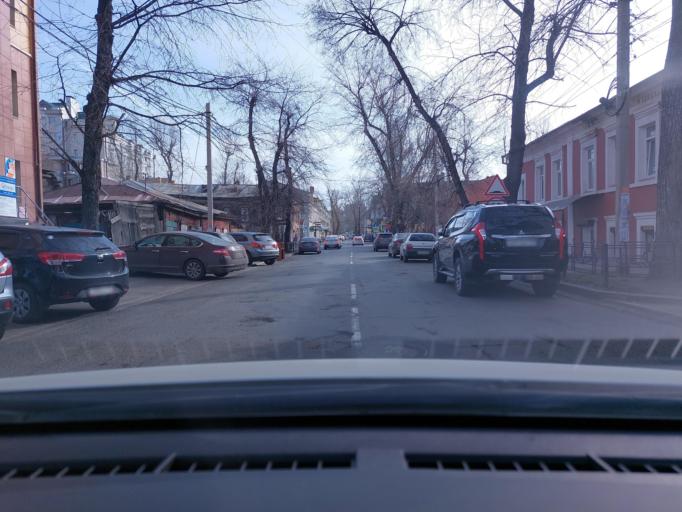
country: RU
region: Irkutsk
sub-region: Irkutskiy Rayon
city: Irkutsk
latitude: 52.2807
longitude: 104.2889
